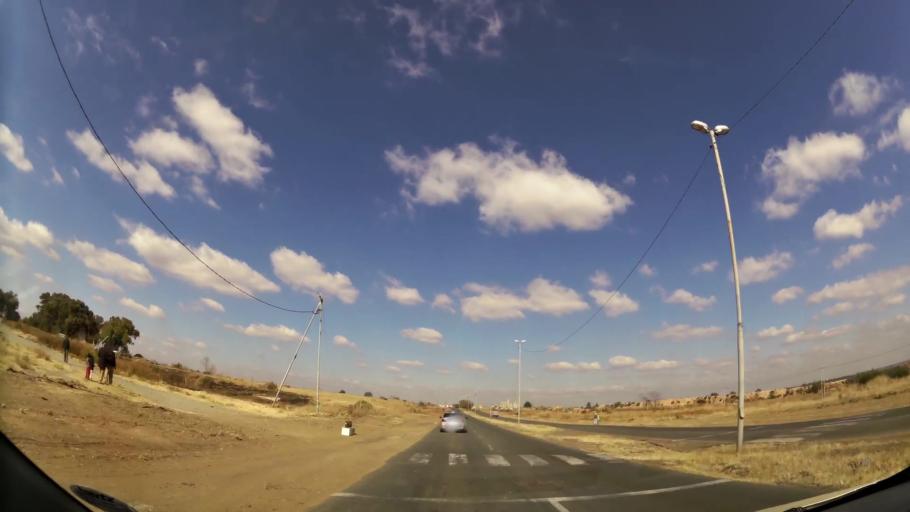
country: ZA
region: Gauteng
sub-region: West Rand District Municipality
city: Krugersdorp
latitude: -26.1314
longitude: 27.8013
